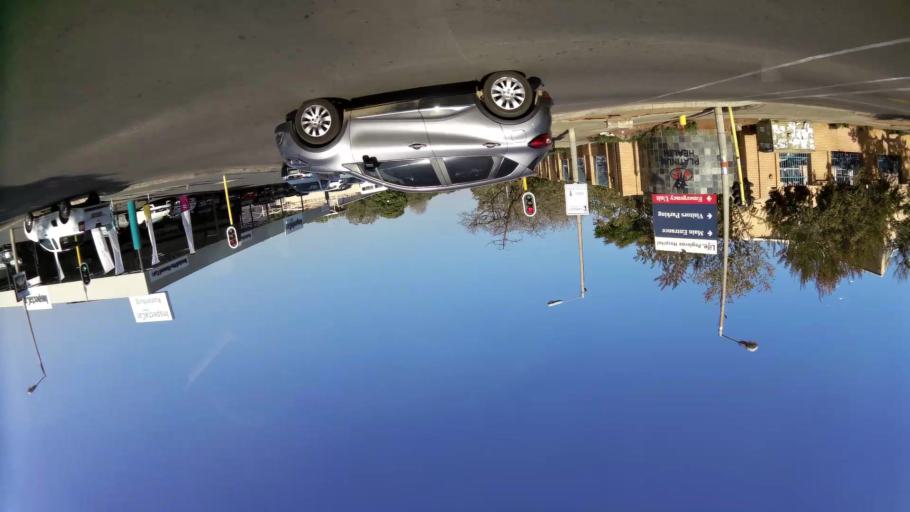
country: ZA
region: North-West
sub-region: Bojanala Platinum District Municipality
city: Rustenburg
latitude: -25.6744
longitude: 27.2410
